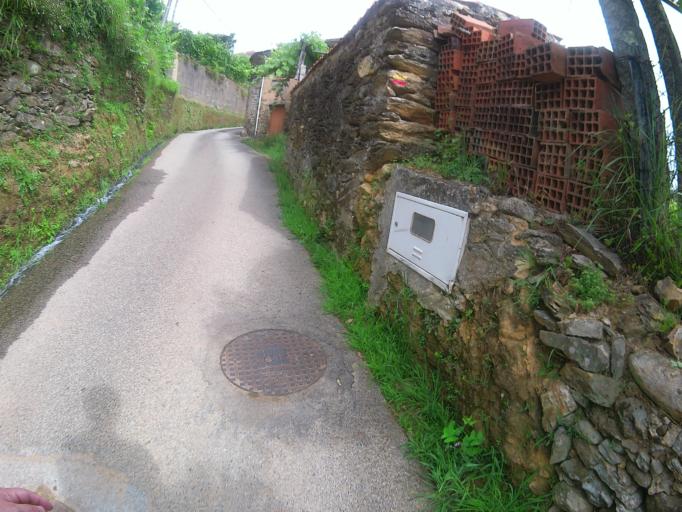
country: PT
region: Aveiro
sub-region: Sever do Vouga
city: Sever do Vouga
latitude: 40.7571
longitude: -8.4230
